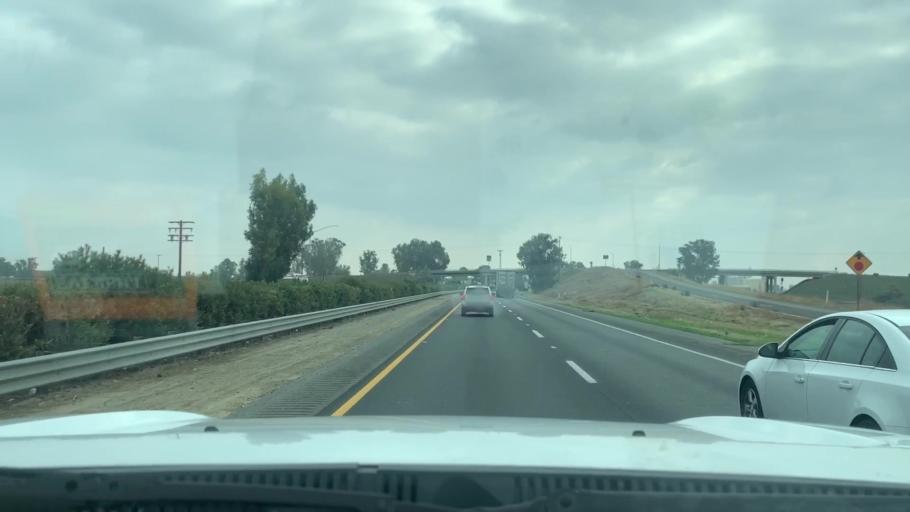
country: US
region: California
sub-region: Tulare County
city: Pixley
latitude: 36.0103
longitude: -119.3029
